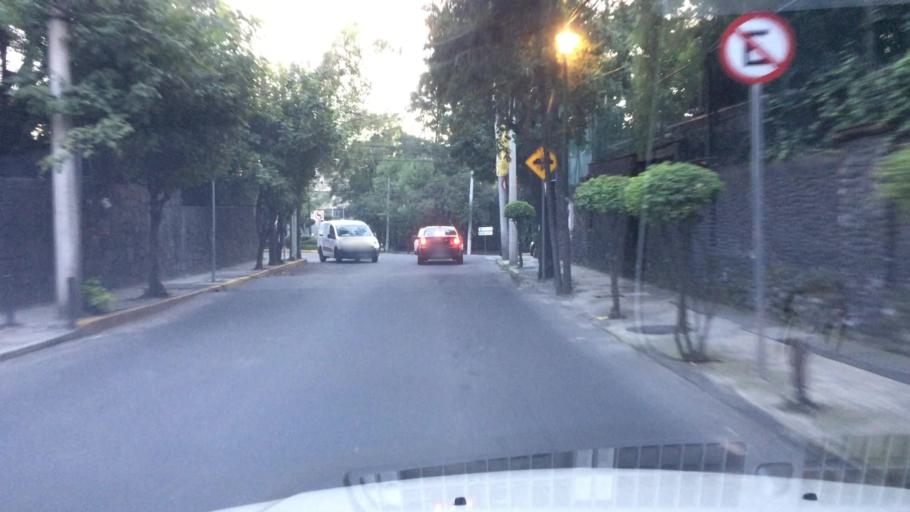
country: MX
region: Mexico City
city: Alvaro Obregon
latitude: 19.3591
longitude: -99.1912
